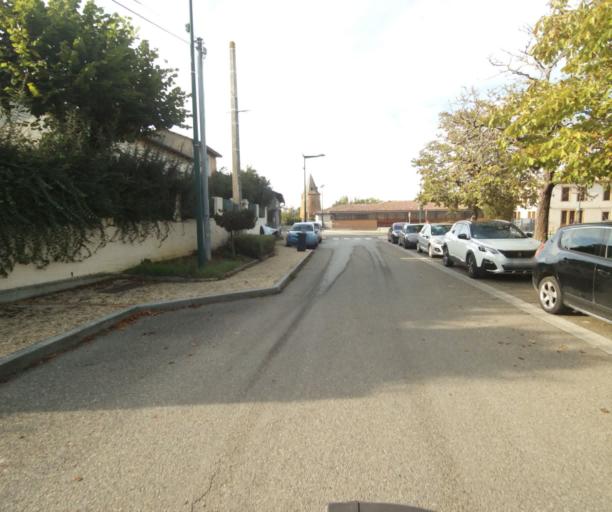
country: FR
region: Midi-Pyrenees
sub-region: Departement du Tarn-et-Garonne
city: Finhan
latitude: 43.8992
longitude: 1.1328
